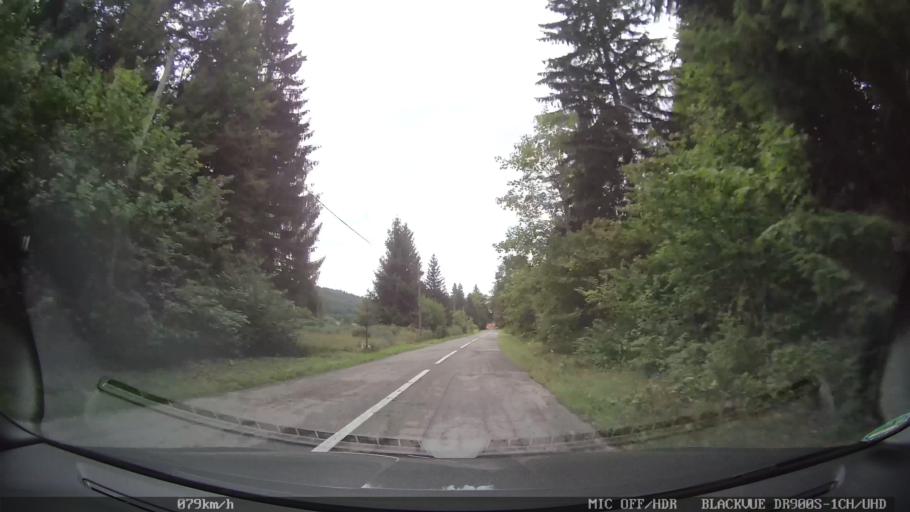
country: HR
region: Licko-Senjska
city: Jezerce
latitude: 44.9529
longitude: 15.5298
